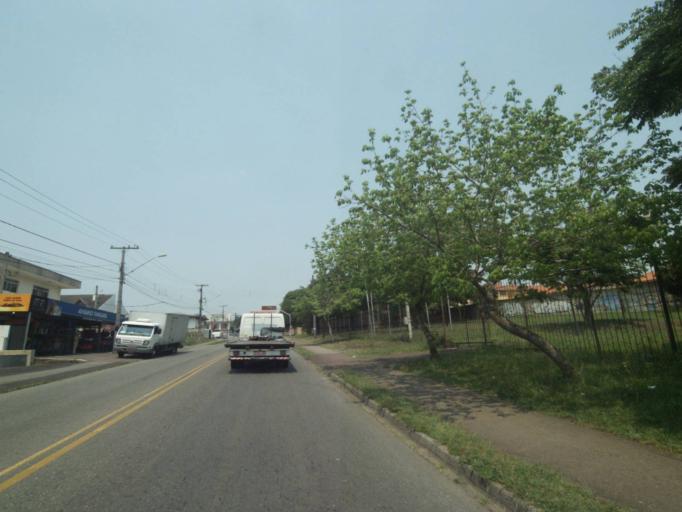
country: BR
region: Parana
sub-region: Sao Jose Dos Pinhais
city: Sao Jose dos Pinhais
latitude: -25.5307
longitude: -49.2417
